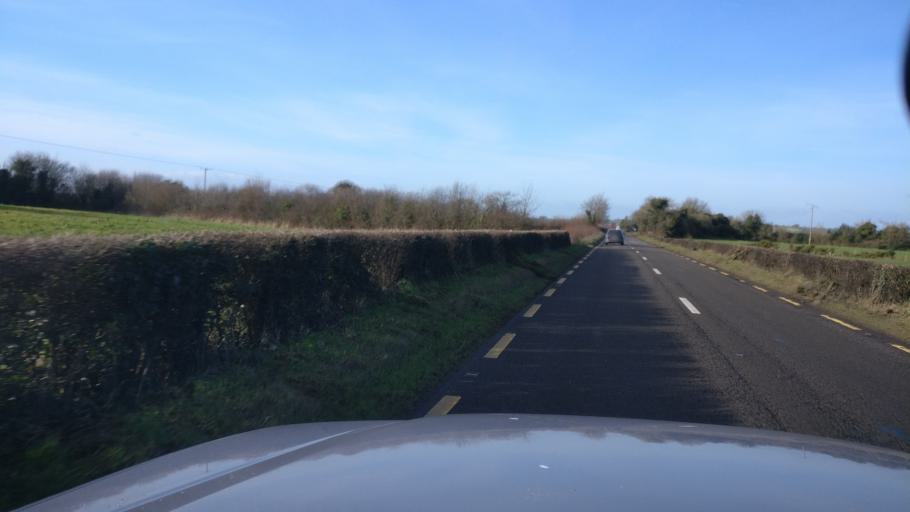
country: IE
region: Leinster
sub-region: Laois
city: Mountmellick
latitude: 53.1730
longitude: -7.3839
